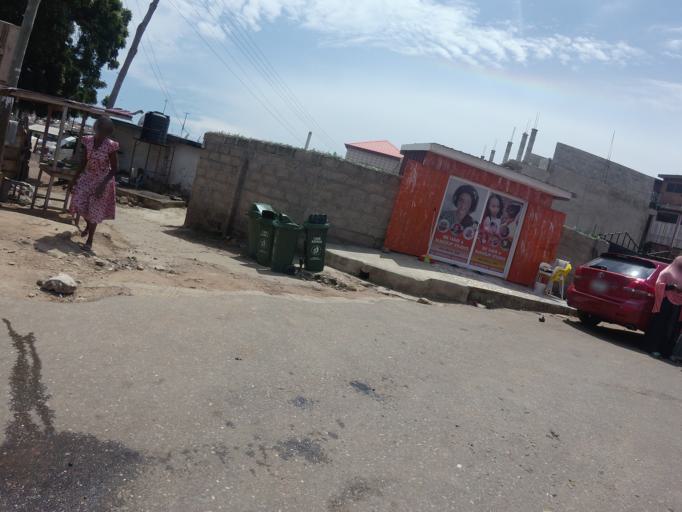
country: GH
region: Greater Accra
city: Accra
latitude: 5.5895
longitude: -0.2029
